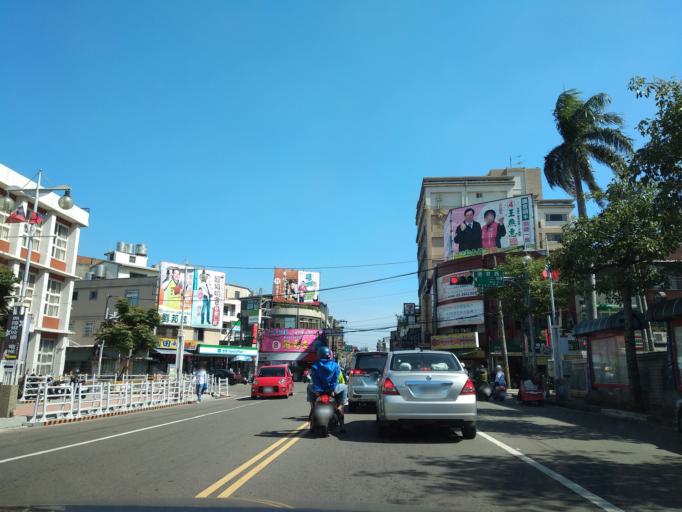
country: TW
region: Taiwan
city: Taoyuan City
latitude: 24.9455
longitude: 121.2186
